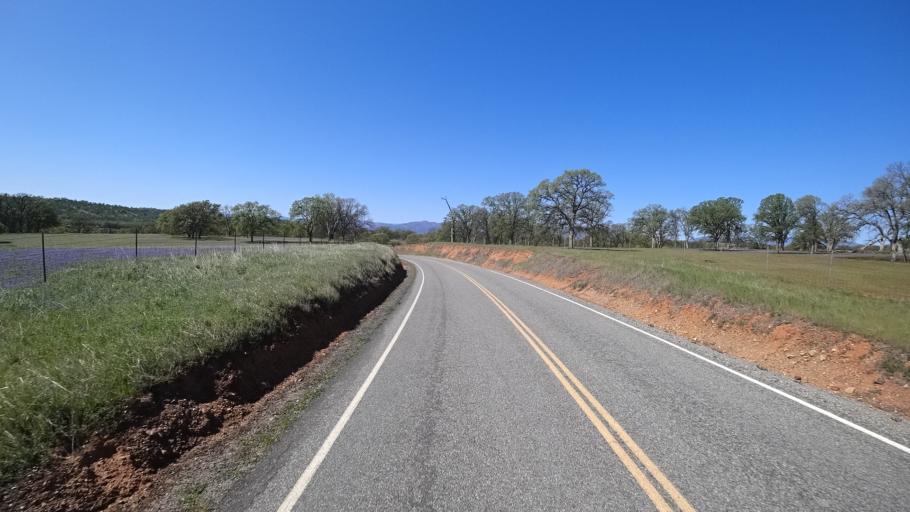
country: US
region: California
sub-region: Tehama County
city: Rancho Tehama Reserve
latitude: 39.8083
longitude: -122.4243
